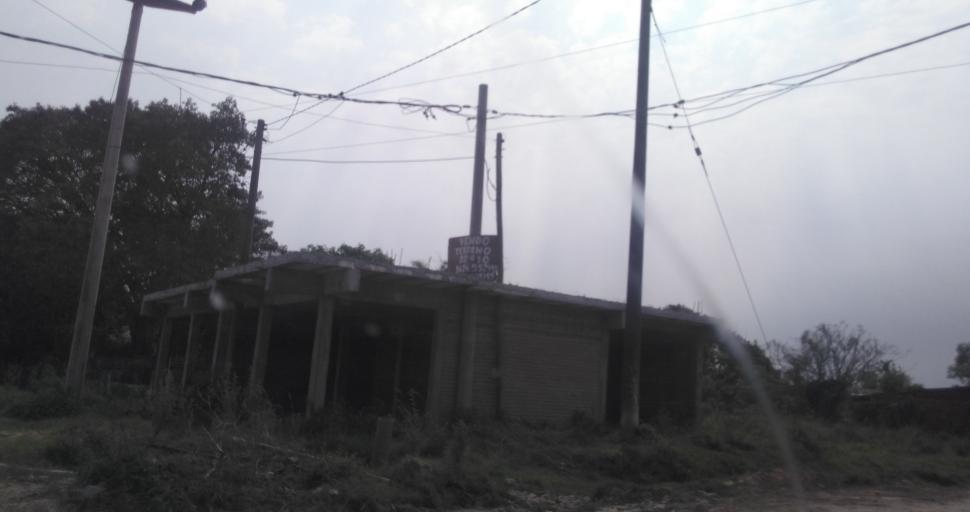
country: AR
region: Chaco
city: Fontana
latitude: -27.4269
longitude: -59.0260
